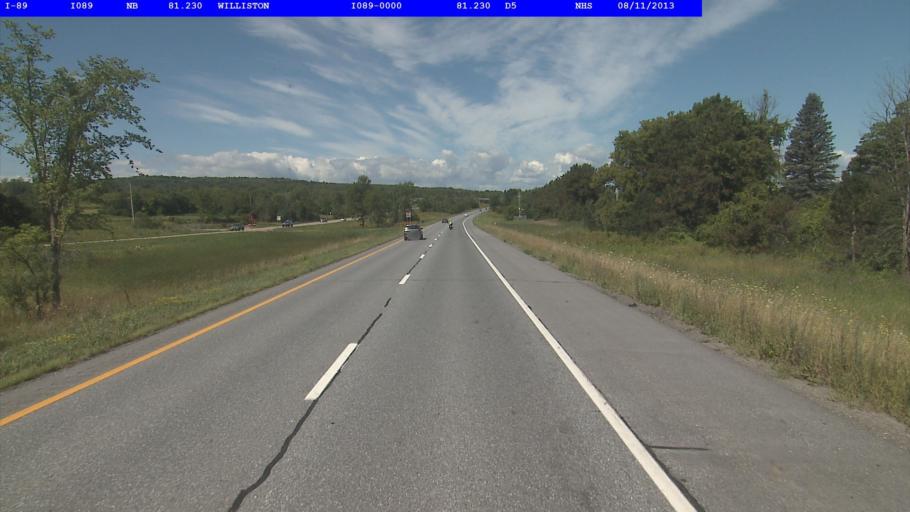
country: US
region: Vermont
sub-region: Chittenden County
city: Williston
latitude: 44.4336
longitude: -73.0604
